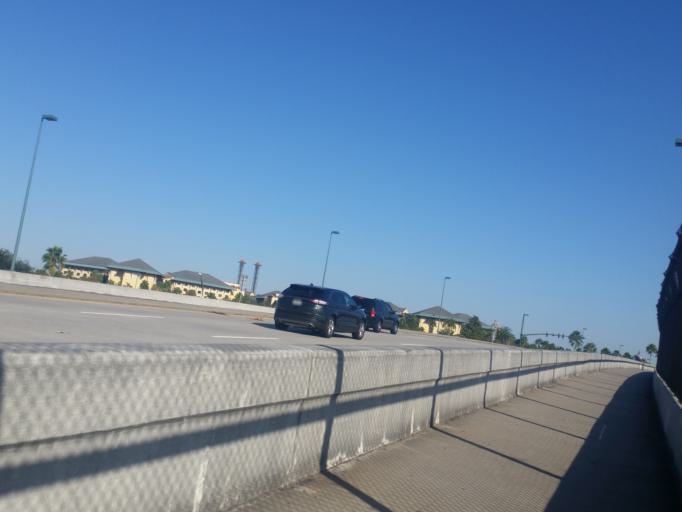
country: US
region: Florida
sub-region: Orange County
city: Tangelo Park
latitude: 28.4656
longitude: -81.4645
